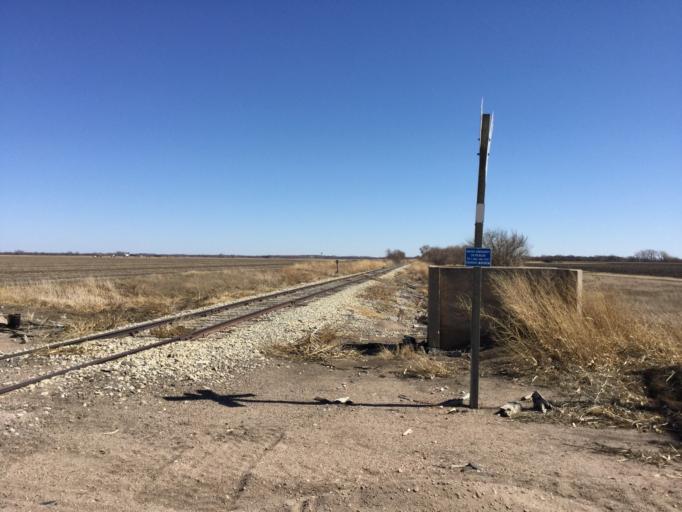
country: US
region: Kansas
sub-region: Pawnee County
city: Larned
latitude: 38.1662
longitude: -99.2233
